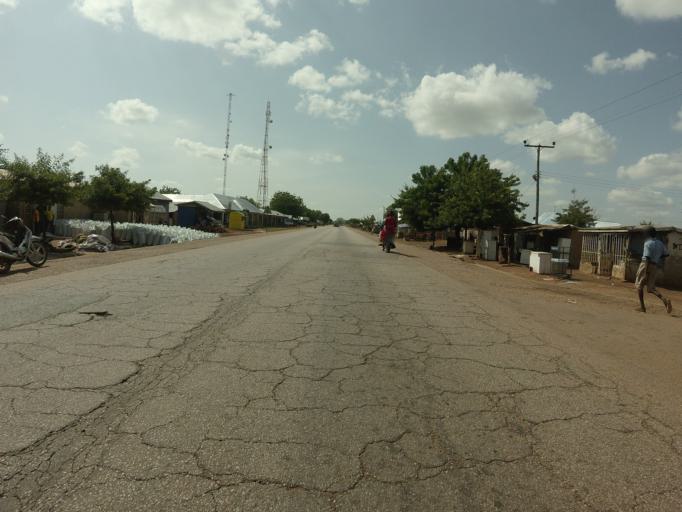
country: GH
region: Northern
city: Savelugu
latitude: 9.8705
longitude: -0.8716
